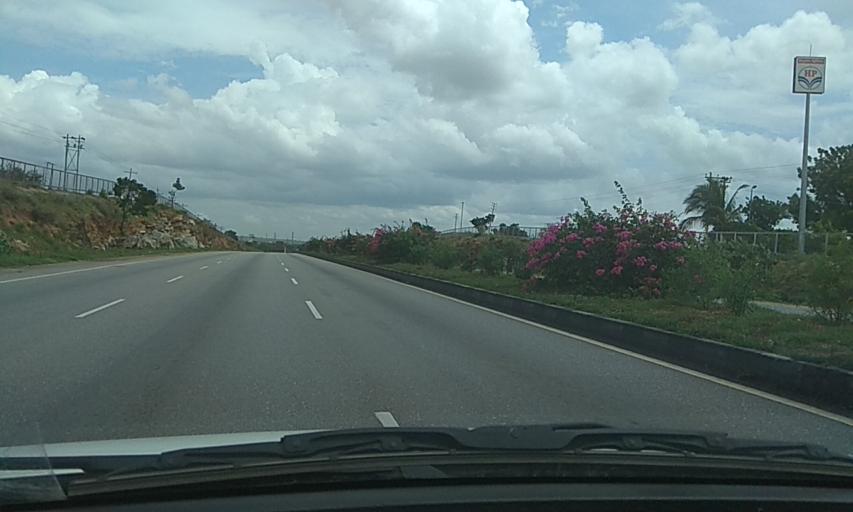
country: IN
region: Karnataka
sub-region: Tumkur
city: Sira
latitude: 13.5870
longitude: 76.9719
